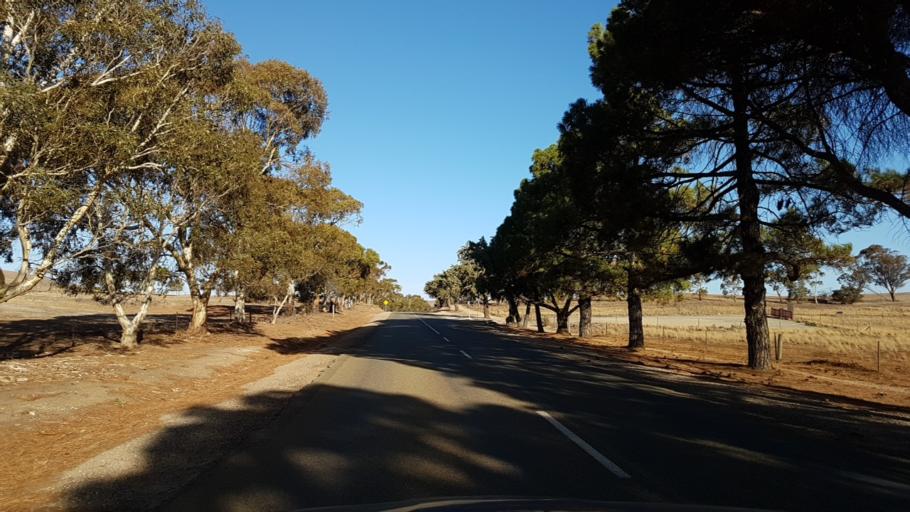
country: AU
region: South Australia
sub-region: Clare and Gilbert Valleys
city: Clare
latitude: -33.6737
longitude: 138.9374
